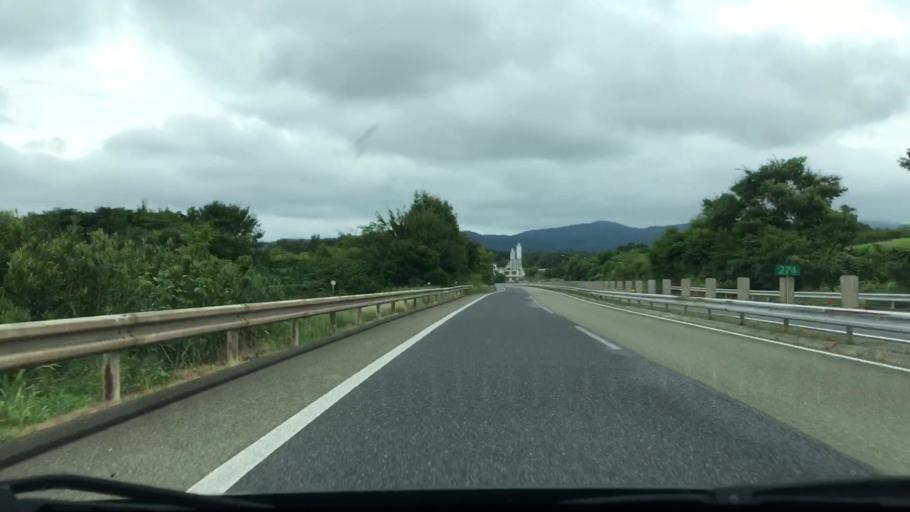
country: JP
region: Hiroshima
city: Shobara
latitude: 34.8331
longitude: 133.0462
